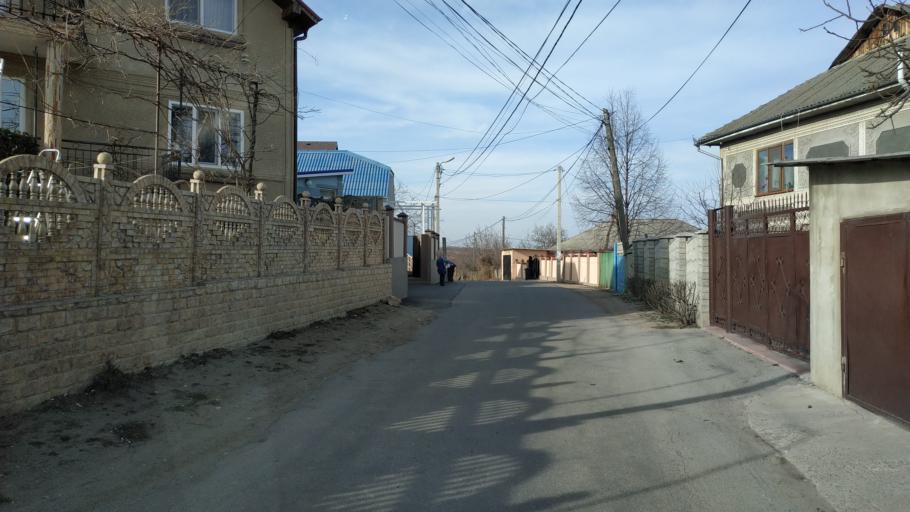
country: MD
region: Chisinau
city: Vatra
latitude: 47.0736
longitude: 28.6717
